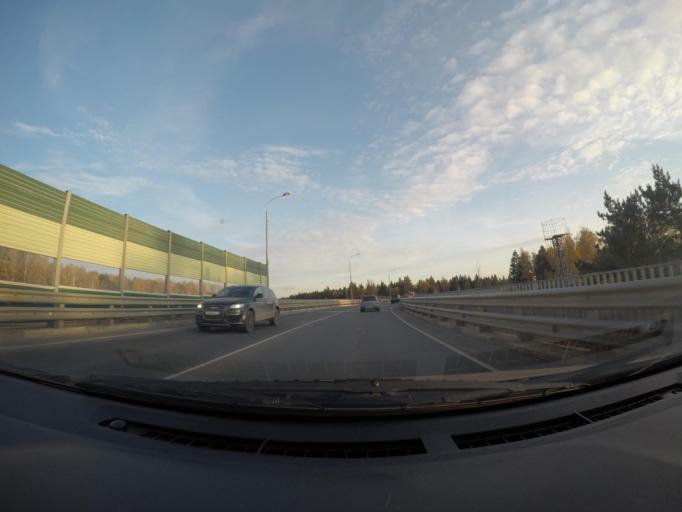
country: RU
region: Moskovskaya
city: Firsanovka
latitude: 55.9590
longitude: 37.2601
